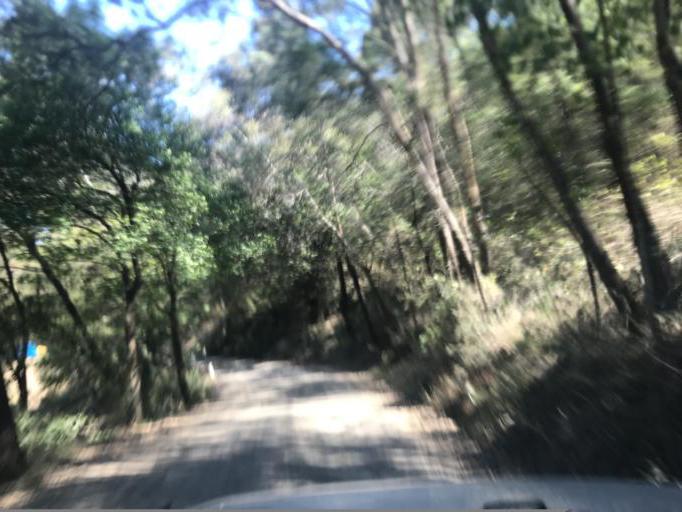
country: AU
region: New South Wales
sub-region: Hawkesbury
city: Pitt Town
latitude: -33.4209
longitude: 150.8959
